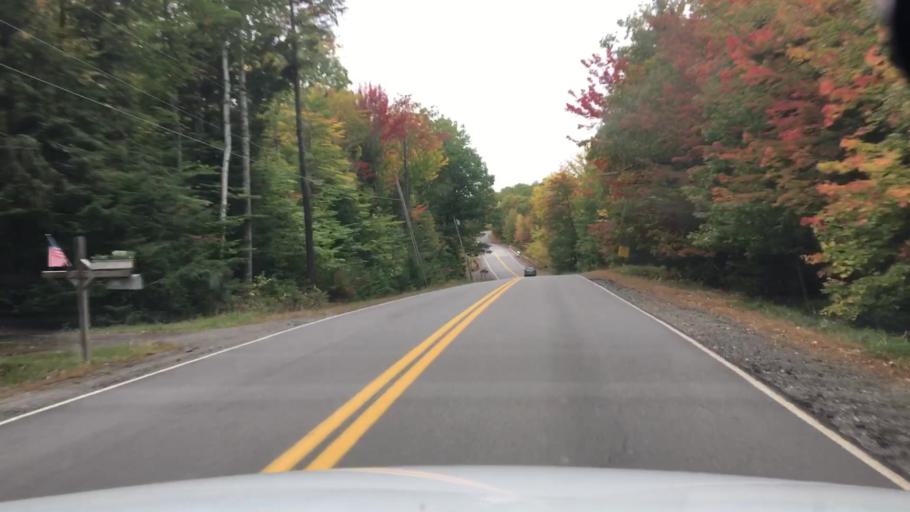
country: US
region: Maine
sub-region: Penobscot County
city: Hudson
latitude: 44.9845
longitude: -68.7904
